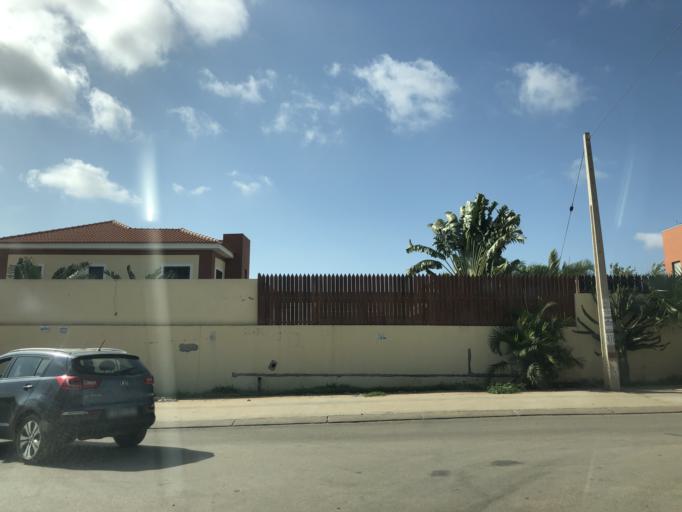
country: AO
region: Luanda
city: Luanda
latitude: -8.9071
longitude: 13.2287
